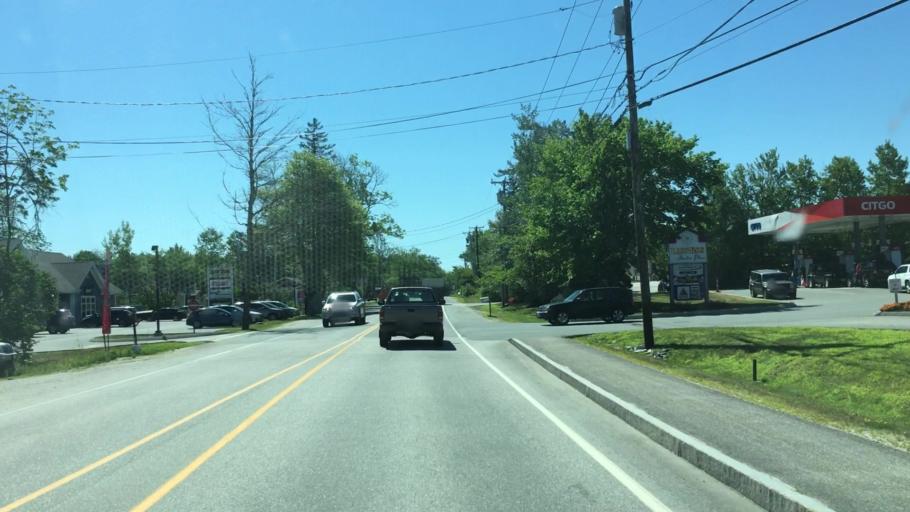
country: US
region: Maine
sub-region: Hancock County
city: Sedgwick
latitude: 44.4076
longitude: -68.5971
